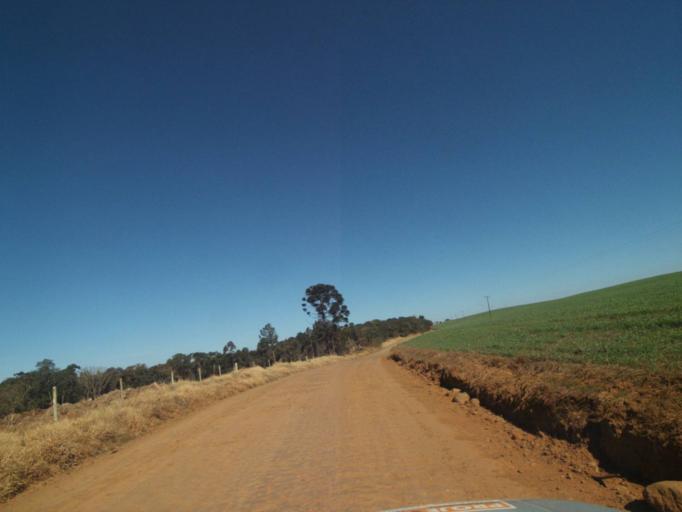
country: BR
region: Parana
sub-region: Tibagi
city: Tibagi
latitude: -24.6135
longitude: -50.6057
